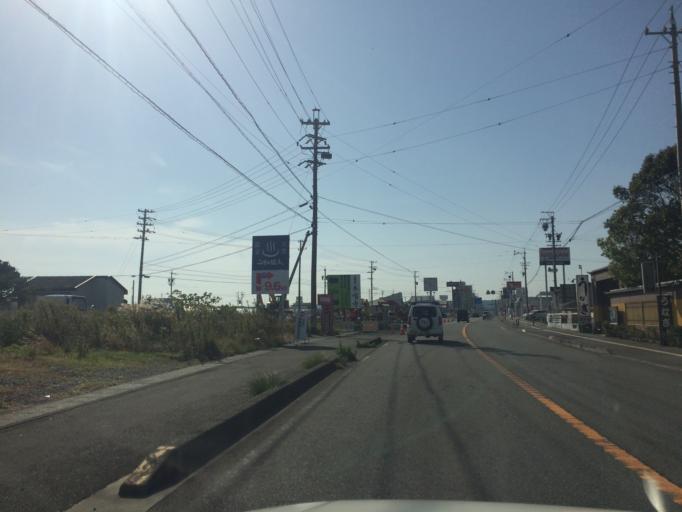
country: JP
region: Shizuoka
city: Sagara
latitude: 34.7420
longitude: 138.2364
